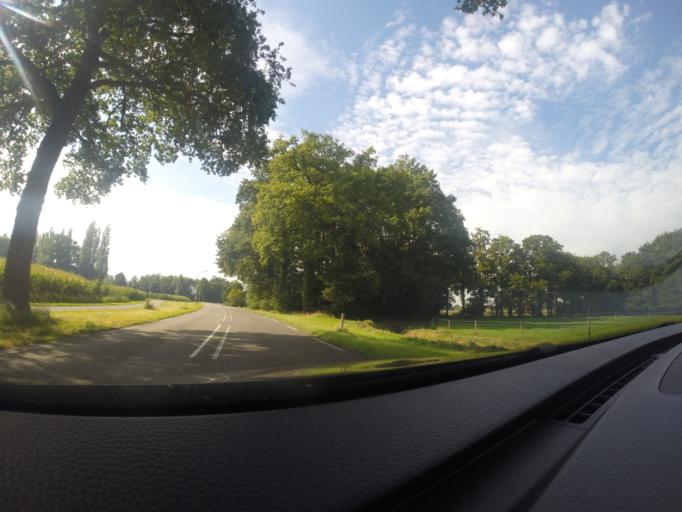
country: NL
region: Gelderland
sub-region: Gemeente Bronckhorst
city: Zelhem
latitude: 51.9664
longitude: 6.3437
